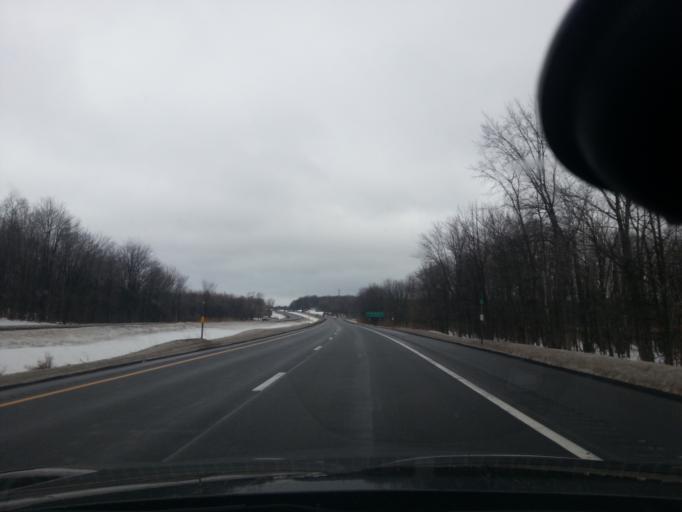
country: US
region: New York
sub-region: Oswego County
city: Central Square
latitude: 43.3122
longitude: -76.1291
